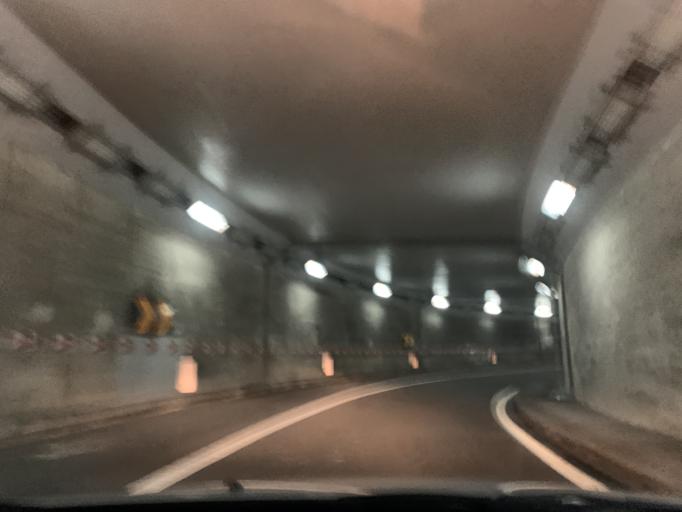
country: JP
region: Yamanashi
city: Otsuki
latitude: 35.6068
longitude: 138.9261
